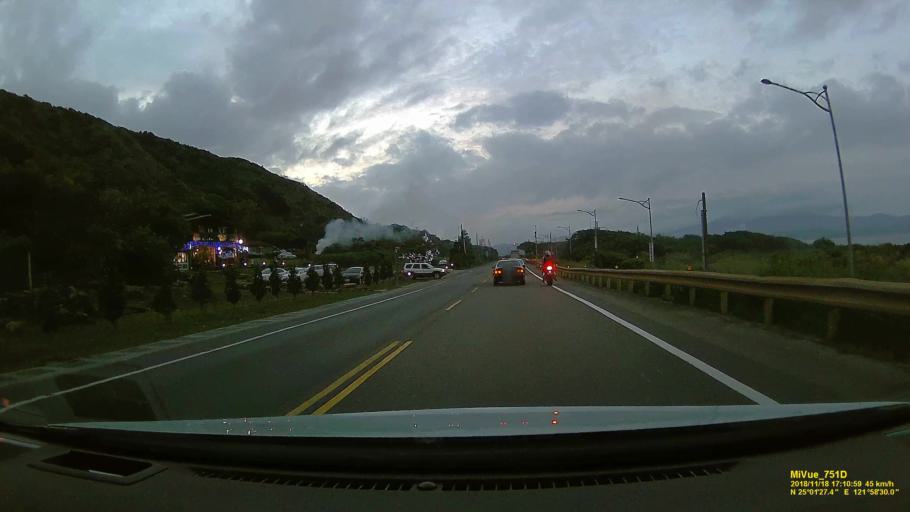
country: TW
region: Taiwan
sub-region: Keelung
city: Keelung
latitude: 25.0243
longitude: 121.9749
